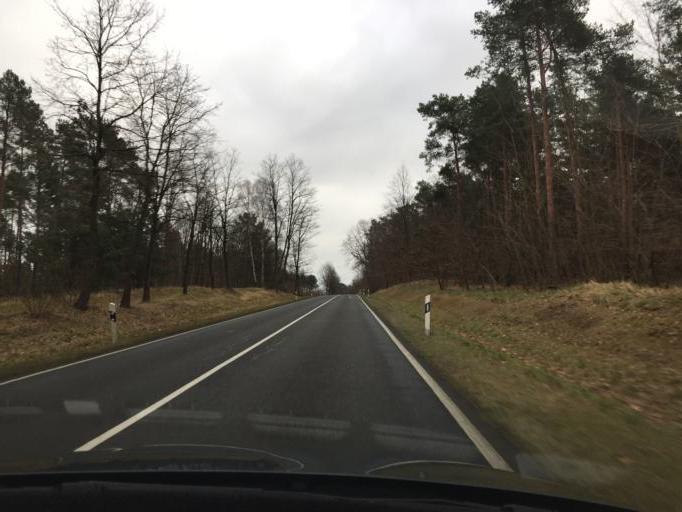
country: DE
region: Brandenburg
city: Ziltendorf
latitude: 52.1485
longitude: 14.5698
